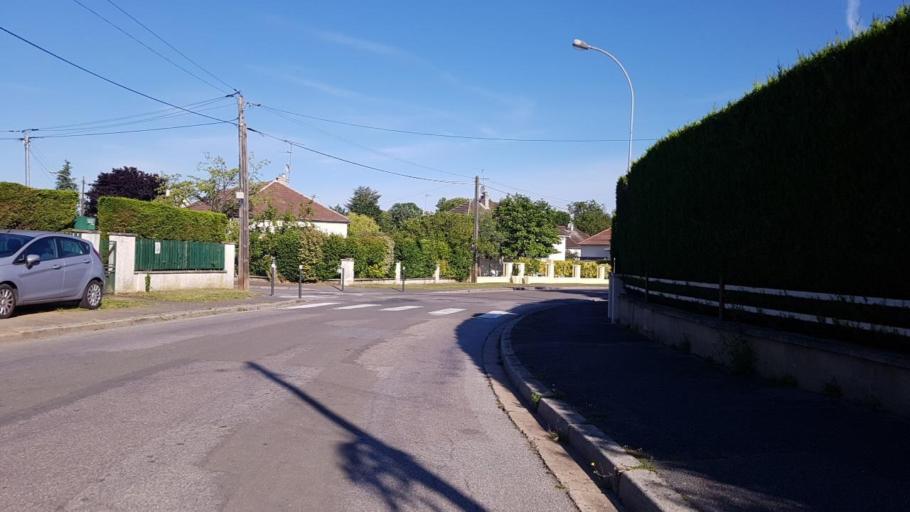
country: FR
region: Picardie
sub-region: Departement de l'Oise
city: Chamant
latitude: 49.2102
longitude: 2.5975
